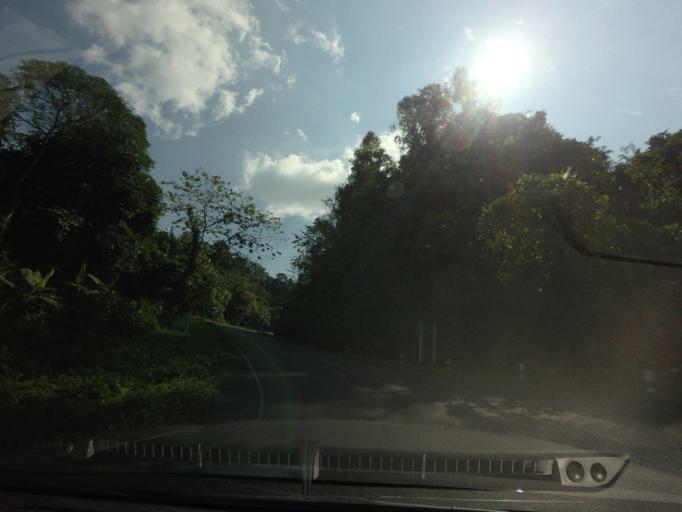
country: TH
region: Nan
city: Bo Kluea
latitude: 19.0599
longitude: 101.0972
